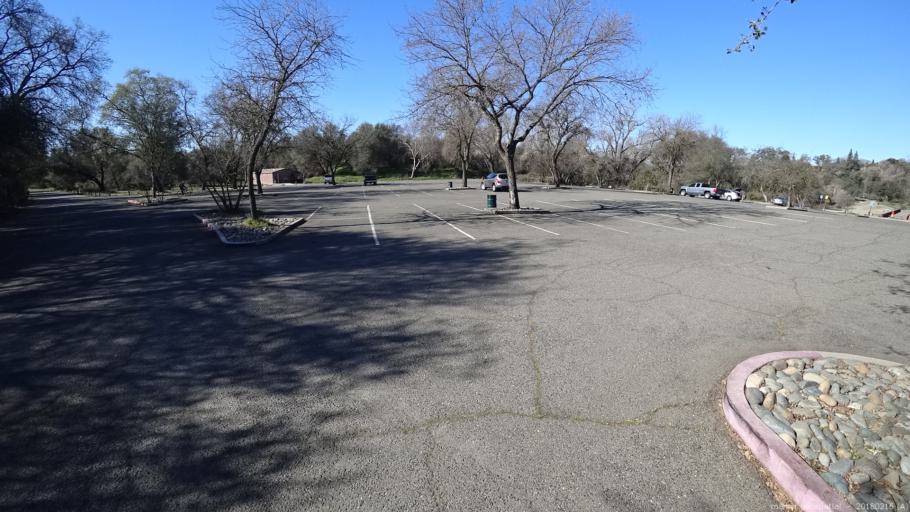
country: US
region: California
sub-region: Sacramento County
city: Fair Oaks
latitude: 38.6316
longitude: -121.2696
